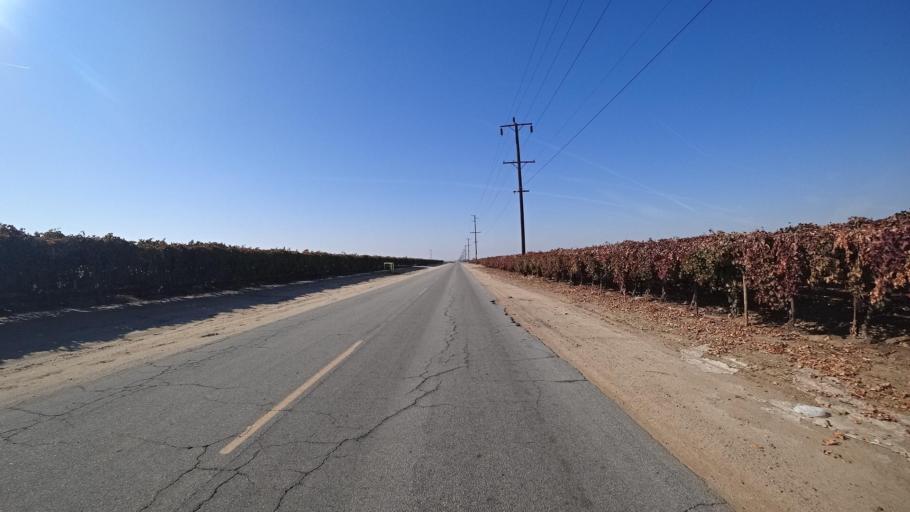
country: US
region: California
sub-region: Kern County
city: McFarland
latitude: 35.7034
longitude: -119.1748
